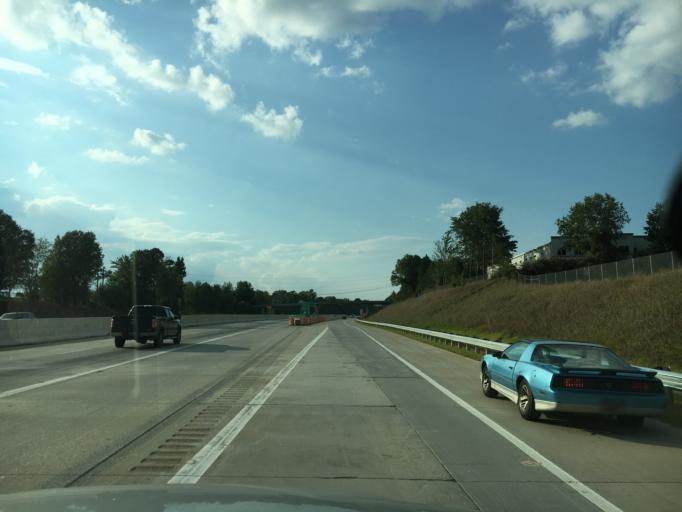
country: US
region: South Carolina
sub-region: Greenville County
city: Mauldin
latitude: 34.8123
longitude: -82.2875
